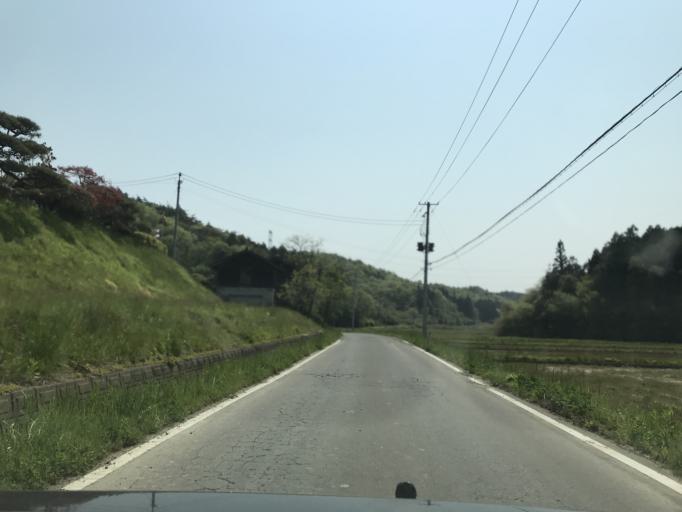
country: JP
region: Iwate
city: Ichinoseki
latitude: 38.8478
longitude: 141.0639
